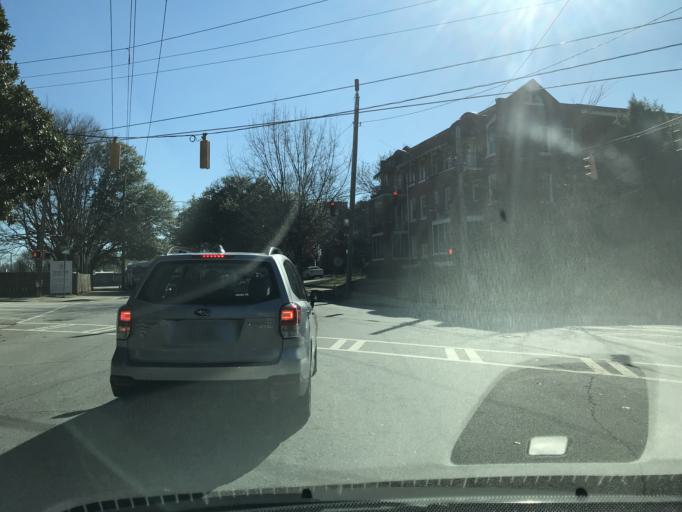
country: US
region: Georgia
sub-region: DeKalb County
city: Druid Hills
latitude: 33.7570
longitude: -84.3558
